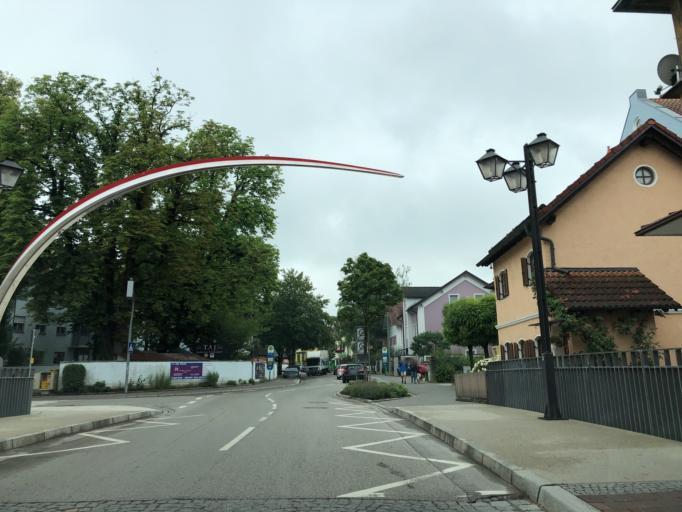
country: DE
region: Bavaria
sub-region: Upper Bavaria
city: Erding
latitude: 48.3033
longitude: 11.9075
